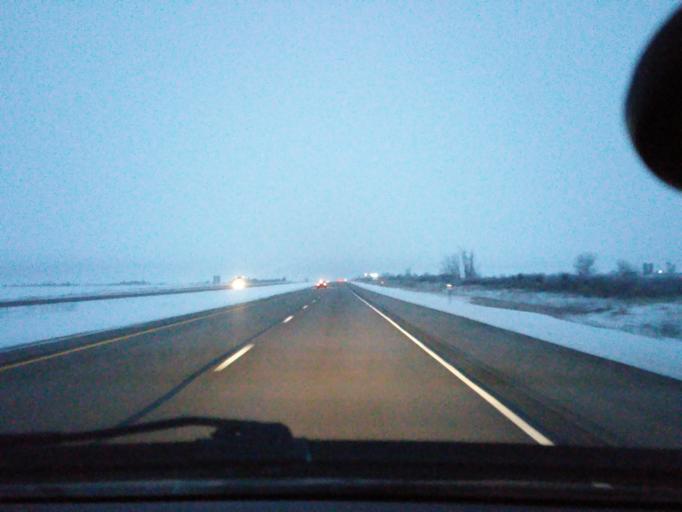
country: US
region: Iowa
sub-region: Worth County
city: Northwood
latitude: 43.4157
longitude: -93.3498
